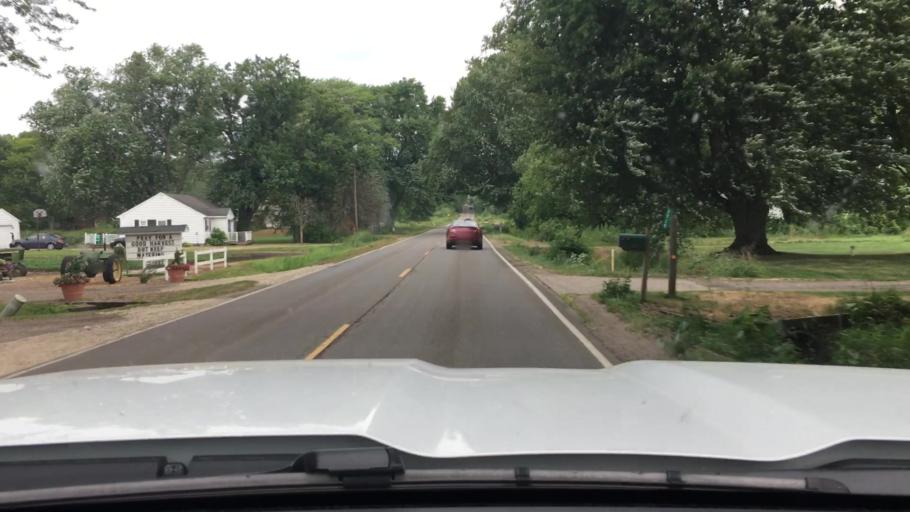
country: US
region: Michigan
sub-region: Kent County
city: Byron Center
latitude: 42.7829
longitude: -85.7306
